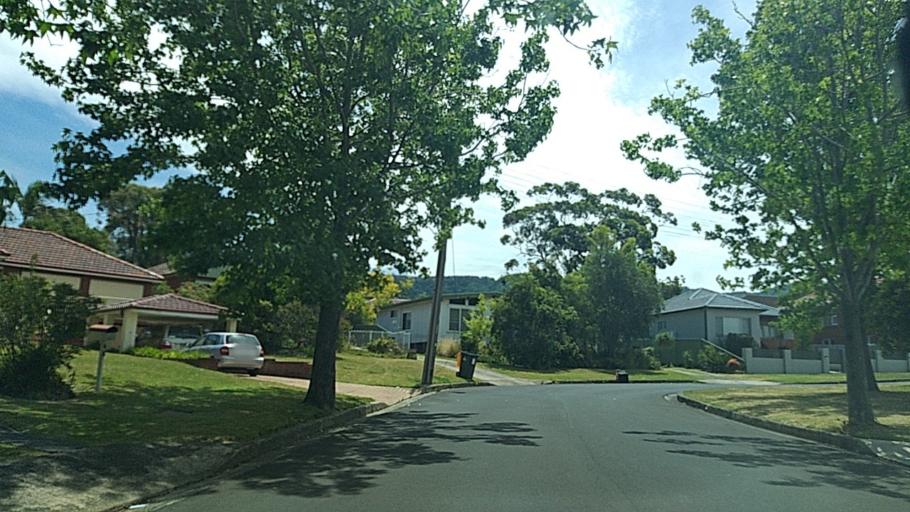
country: AU
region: New South Wales
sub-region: Wollongong
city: Mount Ousley
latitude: -34.3936
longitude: 150.8829
